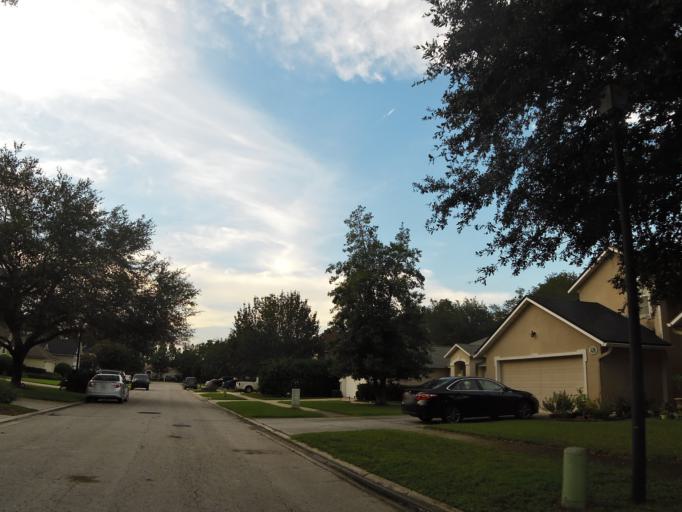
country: US
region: Florida
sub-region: Saint Johns County
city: Palm Valley
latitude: 30.2115
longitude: -81.5163
